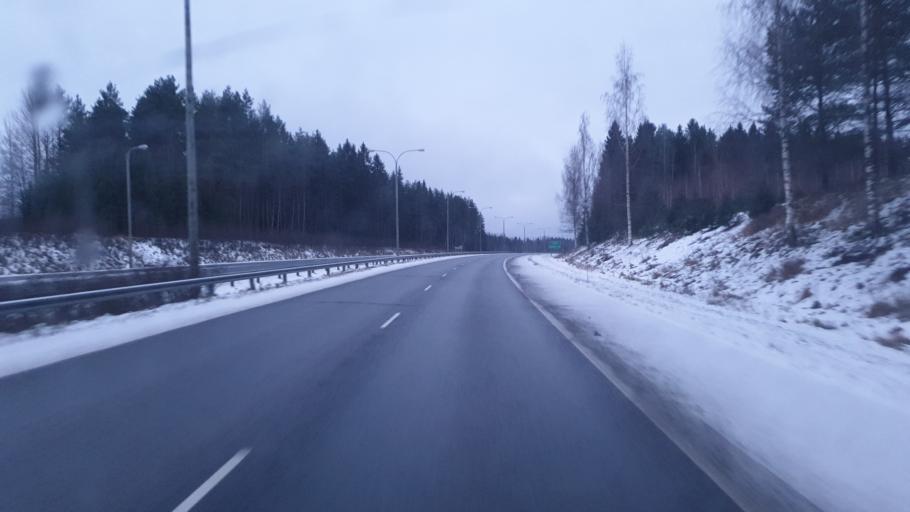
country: FI
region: Northern Savo
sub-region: Kuopio
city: Siilinjaervi
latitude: 63.0549
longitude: 27.6708
